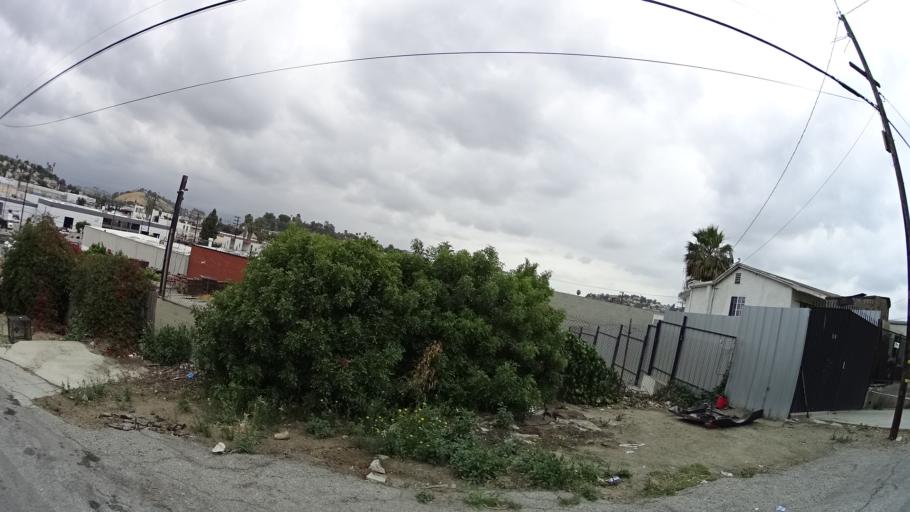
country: US
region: California
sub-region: Los Angeles County
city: Belvedere
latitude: 34.0589
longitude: -118.1832
